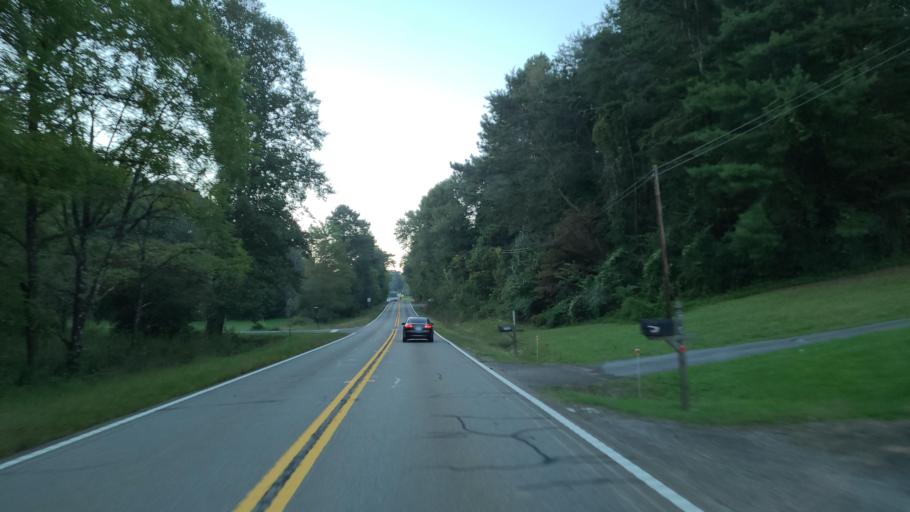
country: US
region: Georgia
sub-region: Gilmer County
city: Ellijay
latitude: 34.7225
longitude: -84.5052
